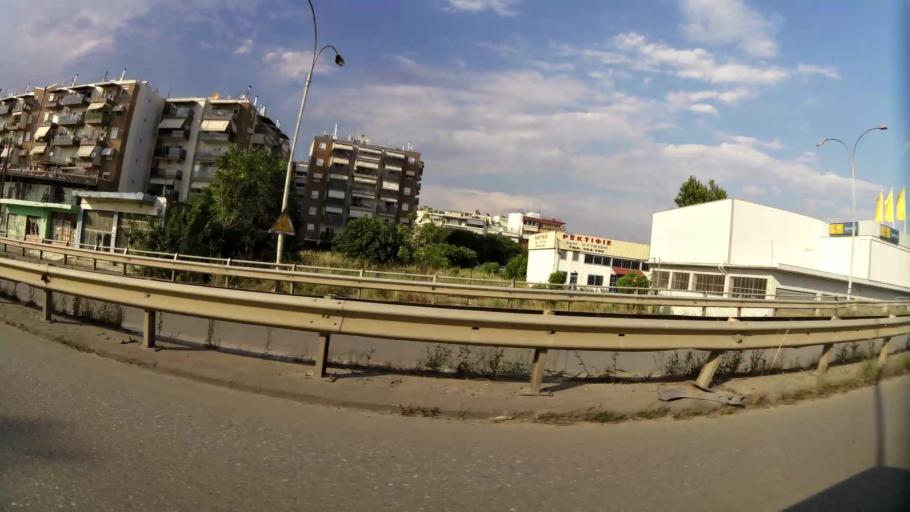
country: GR
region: Central Macedonia
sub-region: Nomos Thessalonikis
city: Menemeni
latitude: 40.6631
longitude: 22.8968
